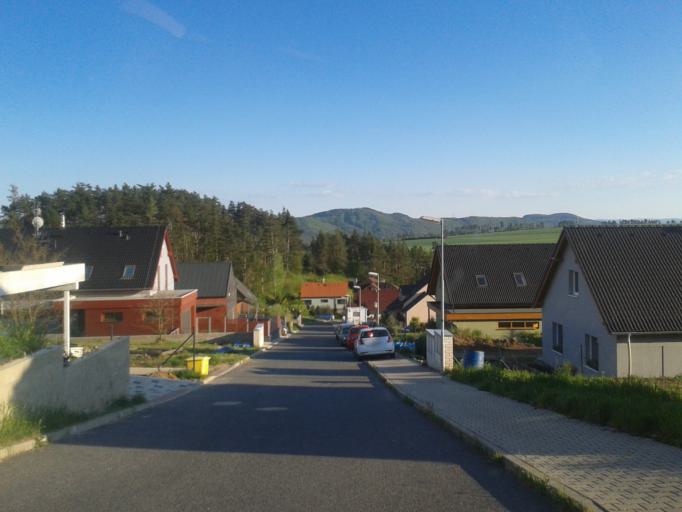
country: CZ
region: Central Bohemia
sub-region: Okres Beroun
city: Kraluv Dvur
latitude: 49.9566
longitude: 14.0217
